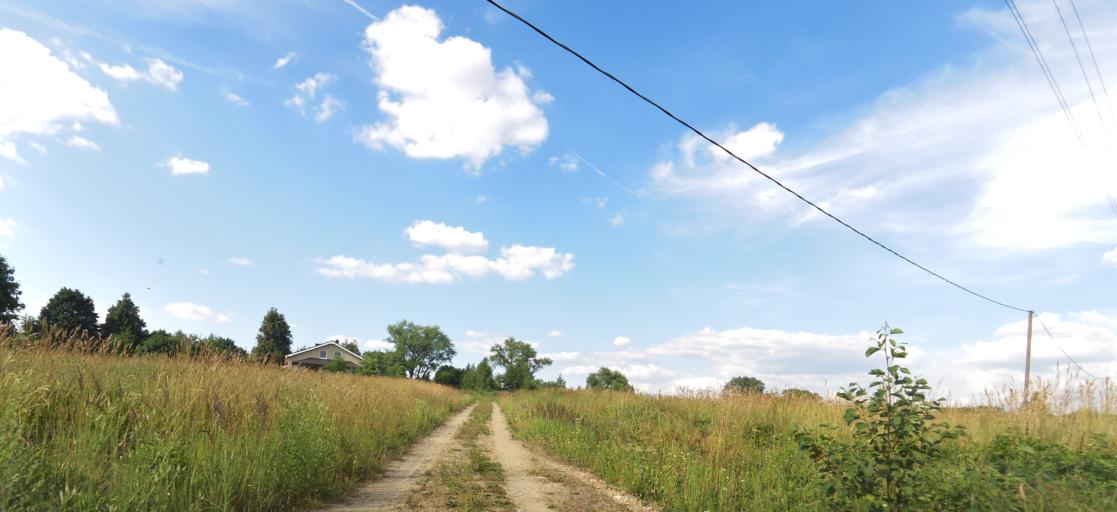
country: LT
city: Skaidiskes
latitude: 54.6381
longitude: 25.3721
